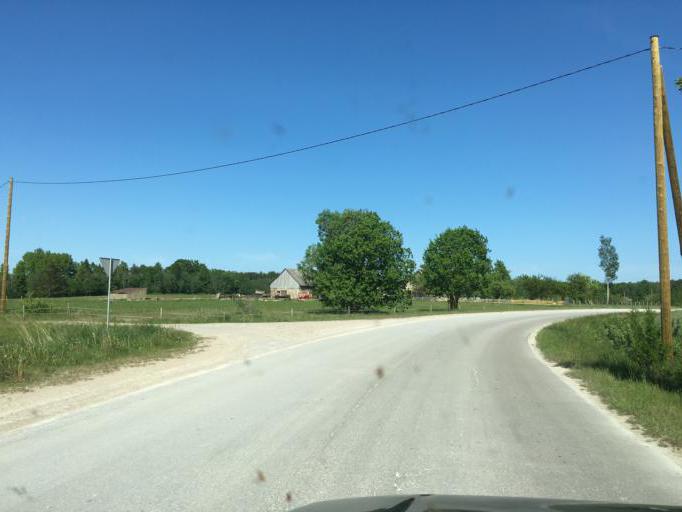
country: LV
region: Dundaga
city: Dundaga
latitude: 57.6086
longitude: 22.4567
